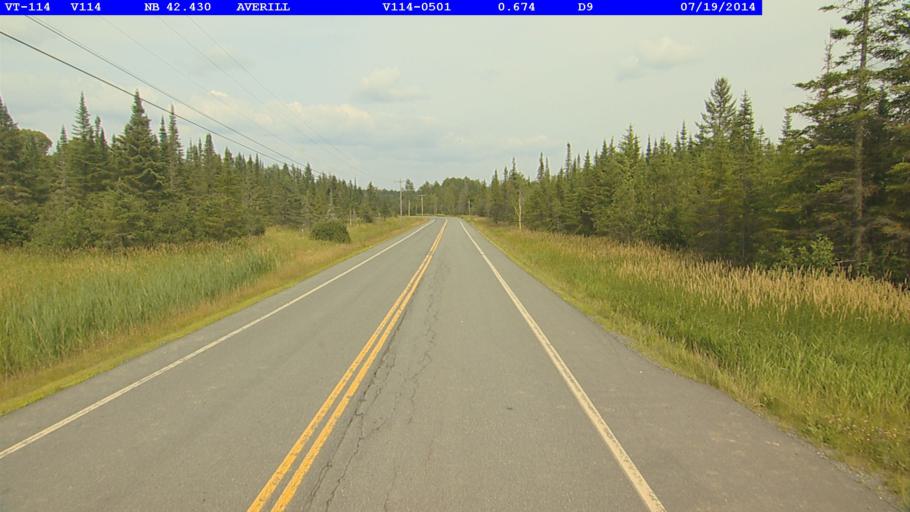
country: CA
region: Quebec
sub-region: Estrie
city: Coaticook
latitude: 45.0027
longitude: -71.6970
